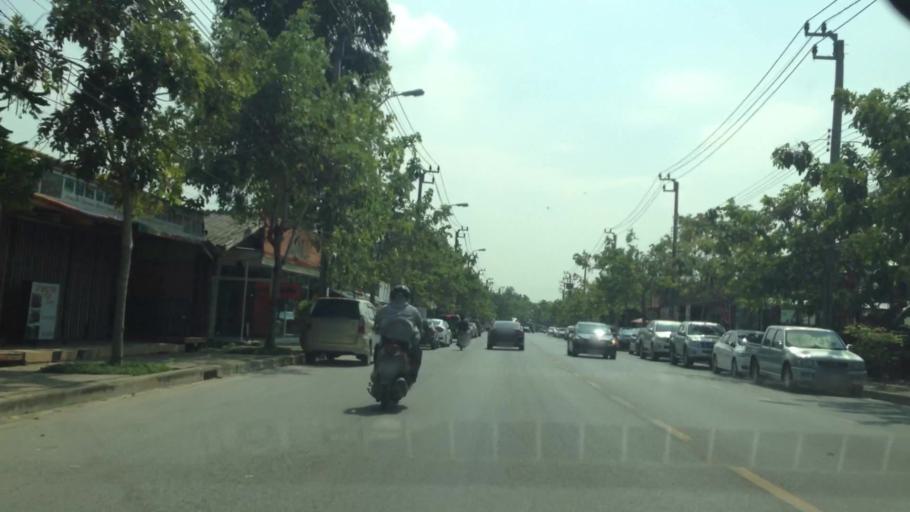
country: TH
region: Bangkok
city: Bang Khen
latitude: 13.8887
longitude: 100.6429
